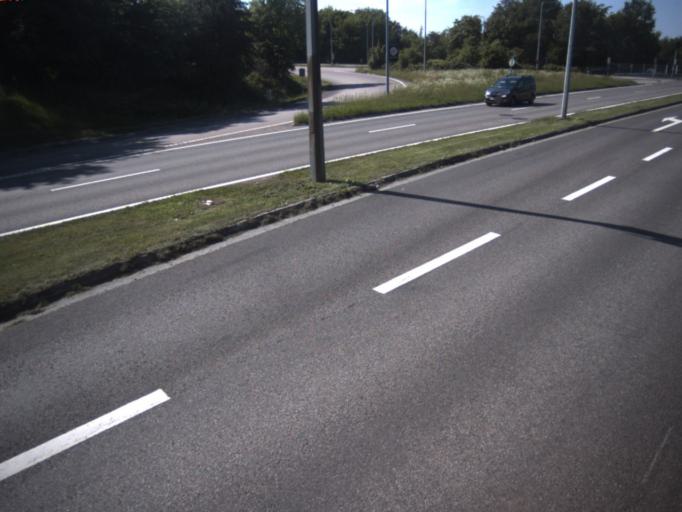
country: SE
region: Skane
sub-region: Helsingborg
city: Gantofta
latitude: 56.0187
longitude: 12.7618
